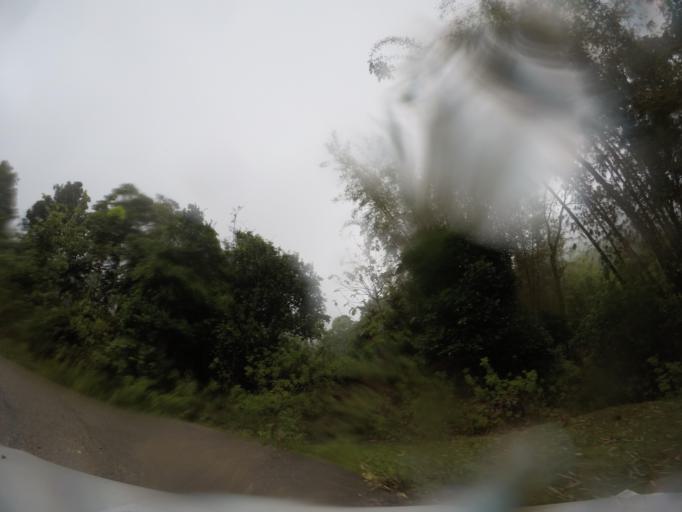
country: TL
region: Baucau
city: Venilale
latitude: -8.6314
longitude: 126.4265
